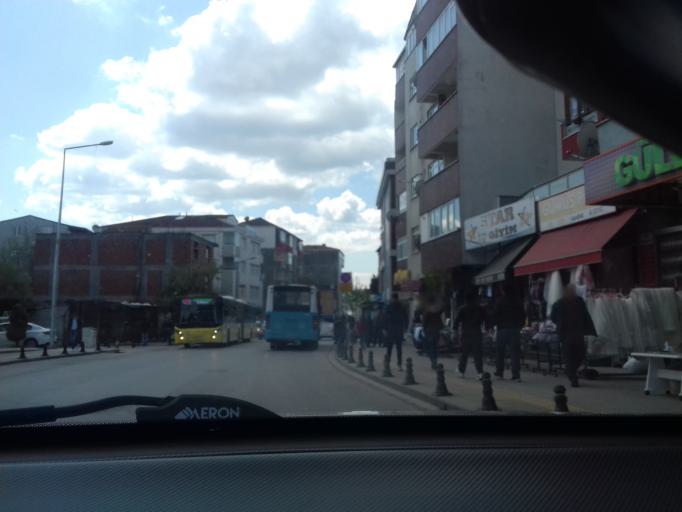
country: TR
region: Istanbul
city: Pendik
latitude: 40.8805
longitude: 29.2868
